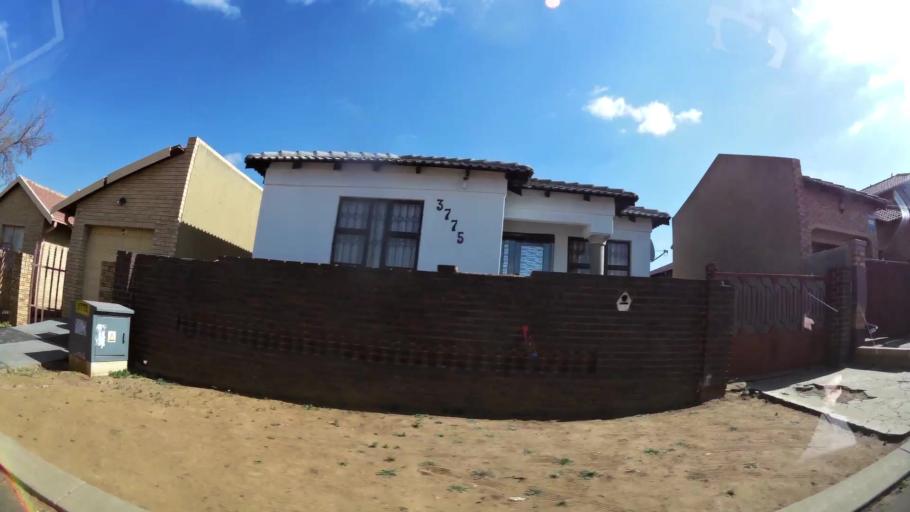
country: ZA
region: Gauteng
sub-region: West Rand District Municipality
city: Krugersdorp
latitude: -26.1649
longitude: 27.7876
